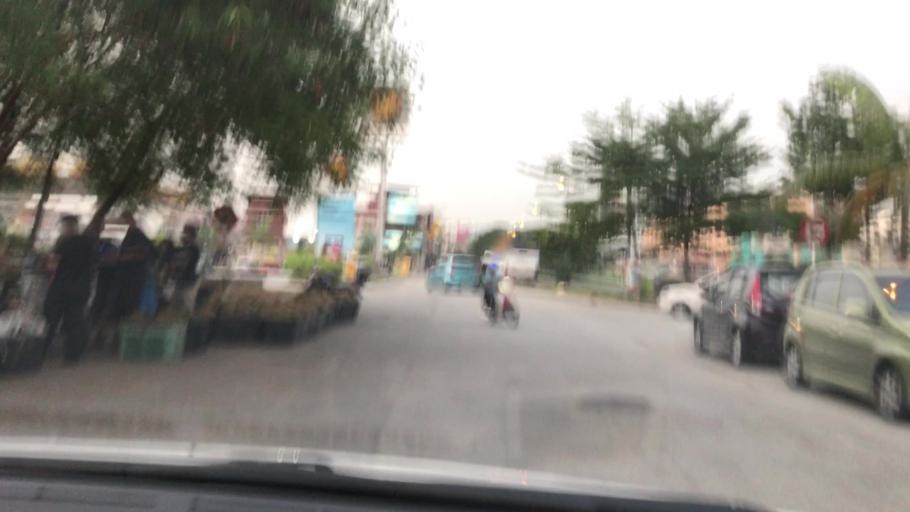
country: MY
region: Putrajaya
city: Putrajaya
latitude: 2.9880
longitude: 101.6705
